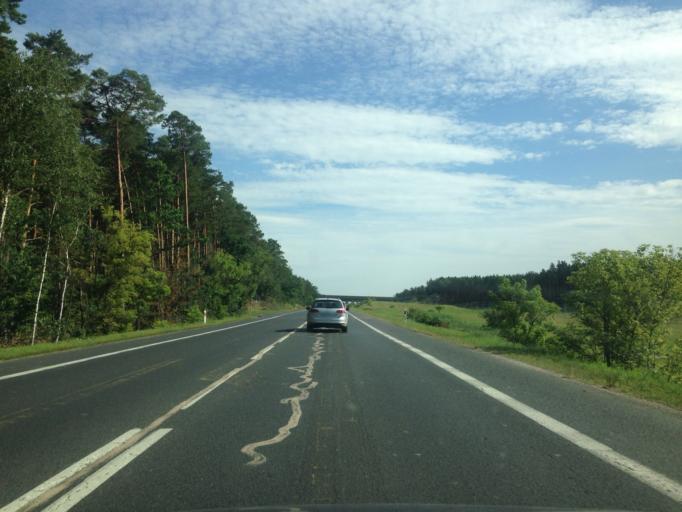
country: PL
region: Kujawsko-Pomorskie
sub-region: Powiat aleksandrowski
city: Aleksandrow Kujawski
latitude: 52.9389
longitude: 18.7007
